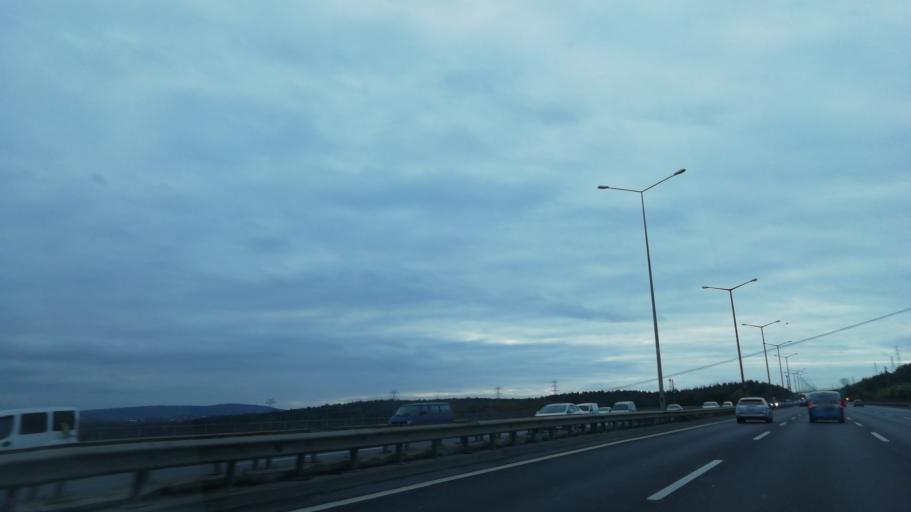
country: TR
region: Istanbul
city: Umraniye
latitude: 41.0752
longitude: 29.1012
